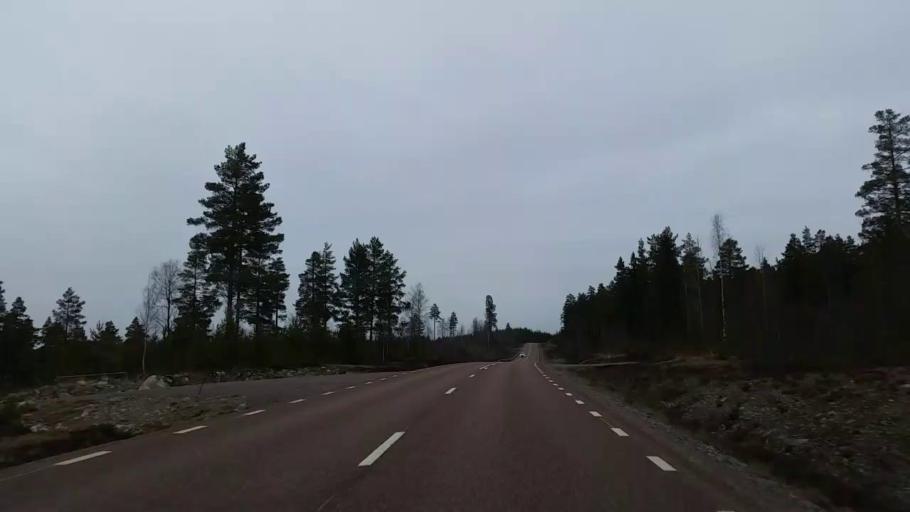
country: SE
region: Gaevleborg
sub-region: Ovanakers Kommun
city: Edsbyn
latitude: 61.2407
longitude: 15.8821
